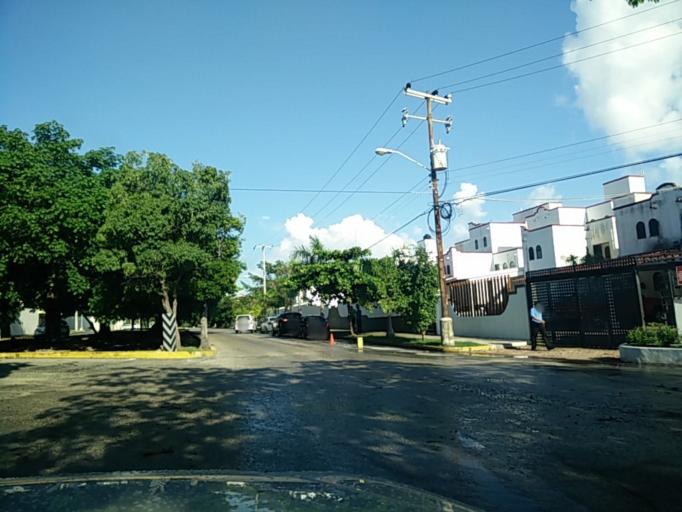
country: MX
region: Quintana Roo
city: Cancun
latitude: 21.1478
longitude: -86.8292
